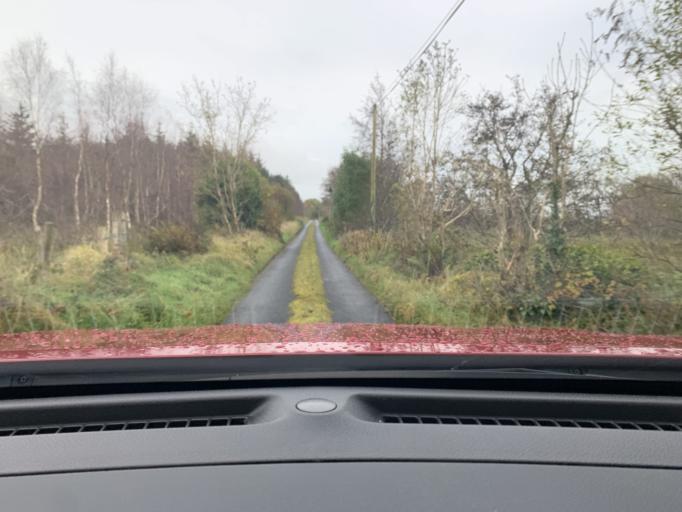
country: IE
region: Connaught
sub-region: Roscommon
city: Ballaghaderreen
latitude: 53.9202
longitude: -8.5590
